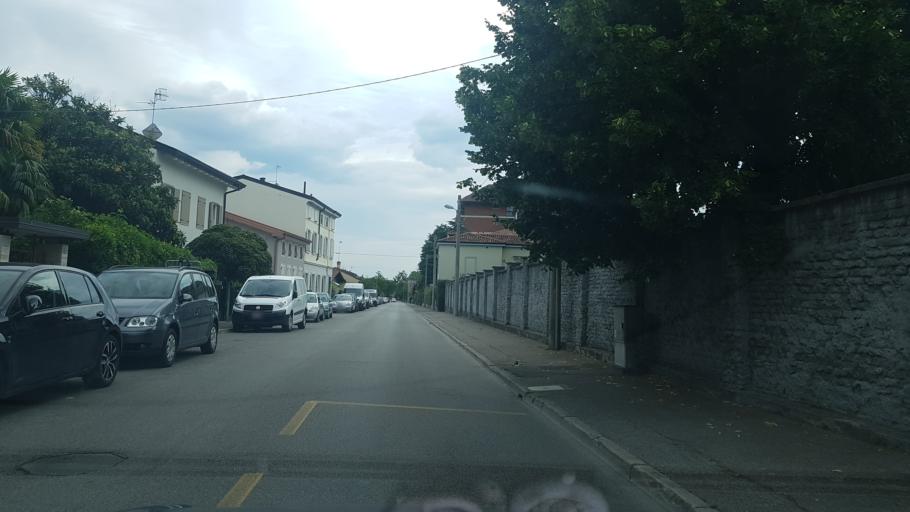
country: IT
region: Friuli Venezia Giulia
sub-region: Provincia di Gorizia
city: Gorizia
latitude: 45.9351
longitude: 13.6201
